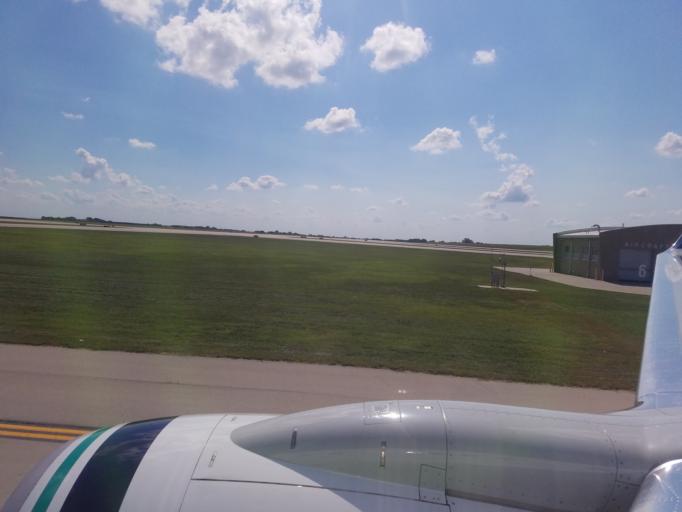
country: US
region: Missouri
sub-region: Platte County
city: Weatherby Lake
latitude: 39.2944
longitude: -94.7233
